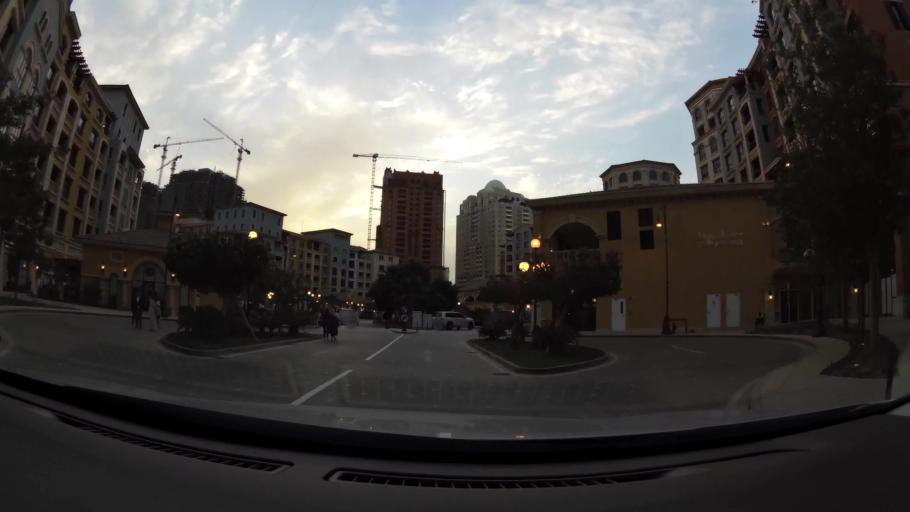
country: QA
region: Baladiyat ad Dawhah
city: Doha
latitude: 25.3694
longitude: 51.5522
